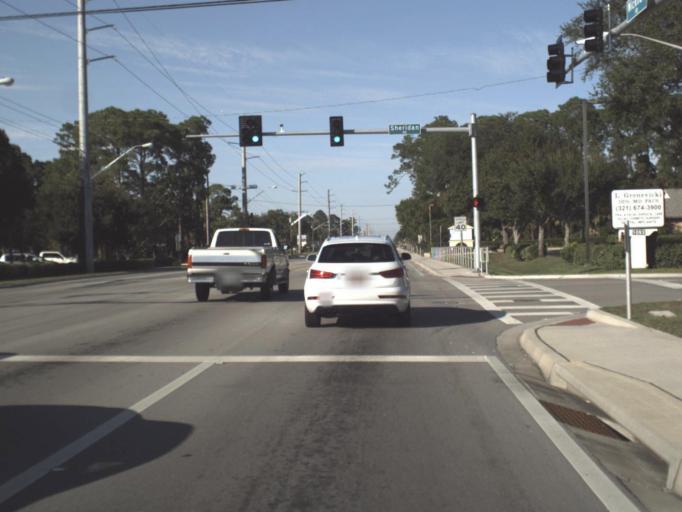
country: US
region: Florida
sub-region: Brevard County
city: June Park
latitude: 28.0887
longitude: -80.6725
